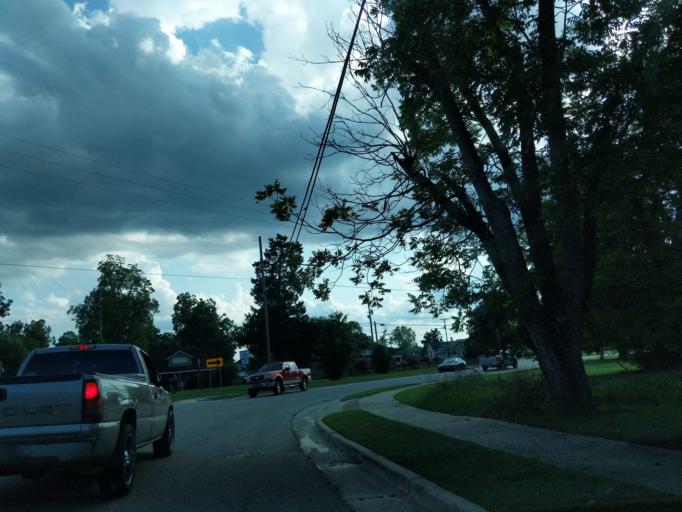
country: US
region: South Carolina
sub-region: Barnwell County
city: Williston
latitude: 33.4032
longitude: -81.4192
